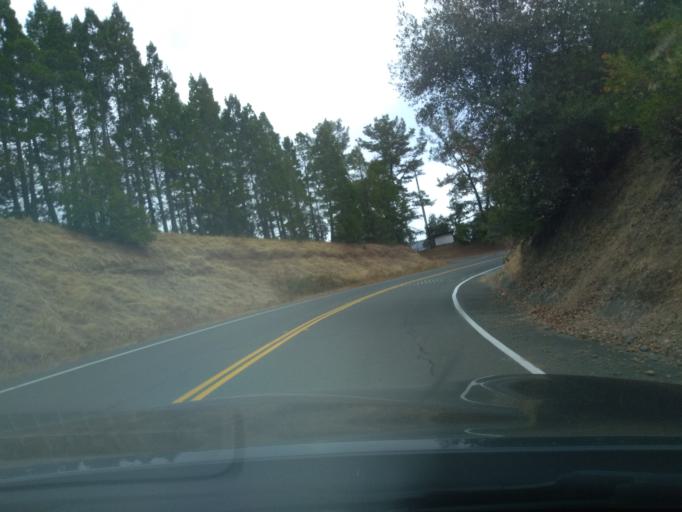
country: US
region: California
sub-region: Mendocino County
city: Ukiah
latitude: 39.2020
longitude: -123.1887
